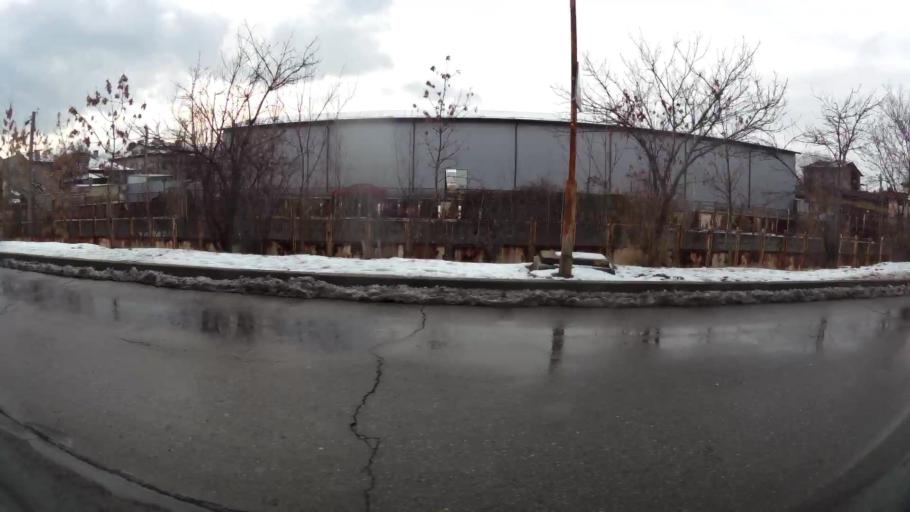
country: BG
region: Sofia-Capital
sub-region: Stolichna Obshtina
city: Sofia
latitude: 42.7037
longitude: 23.3772
